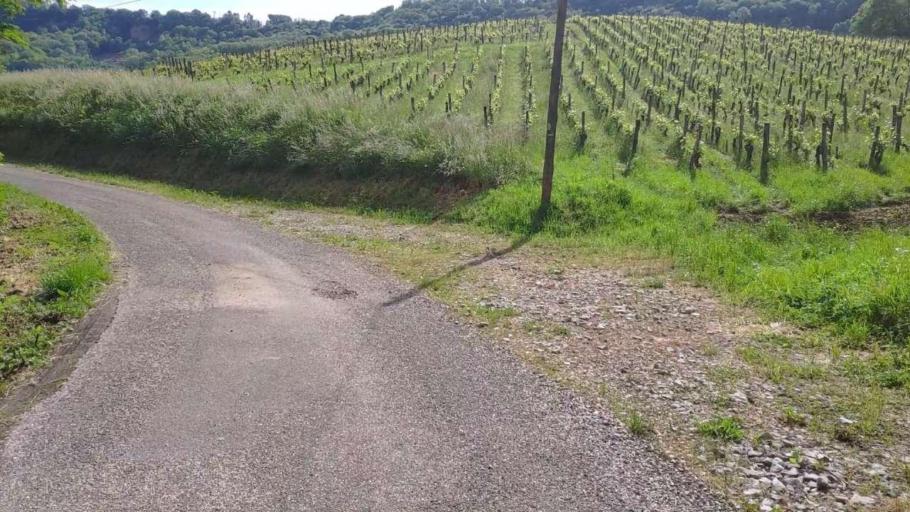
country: FR
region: Franche-Comte
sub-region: Departement du Jura
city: Perrigny
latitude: 46.7602
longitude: 5.6256
